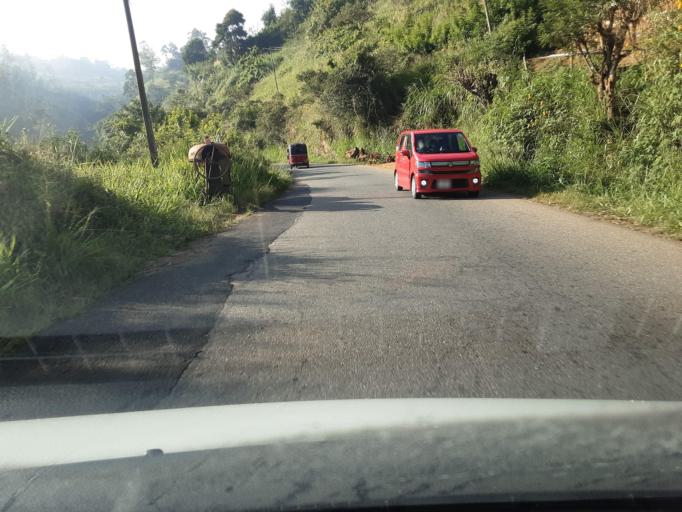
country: LK
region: Uva
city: Haputale
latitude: 6.9083
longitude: 80.9231
